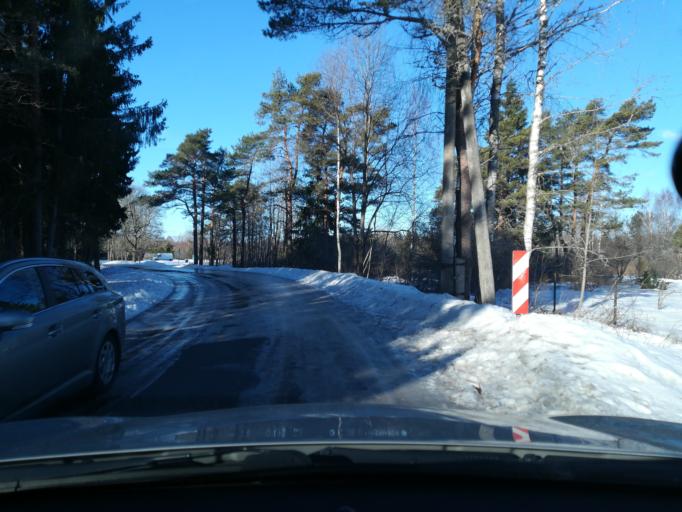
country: EE
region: Raplamaa
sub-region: Kohila vald
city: Kohila
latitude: 59.2291
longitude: 24.7511
